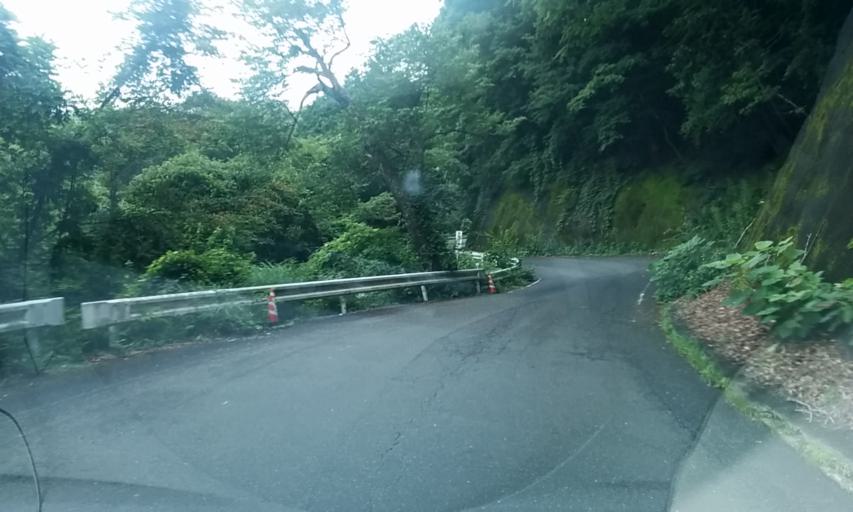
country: JP
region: Kyoto
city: Kameoka
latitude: 35.0523
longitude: 135.4260
